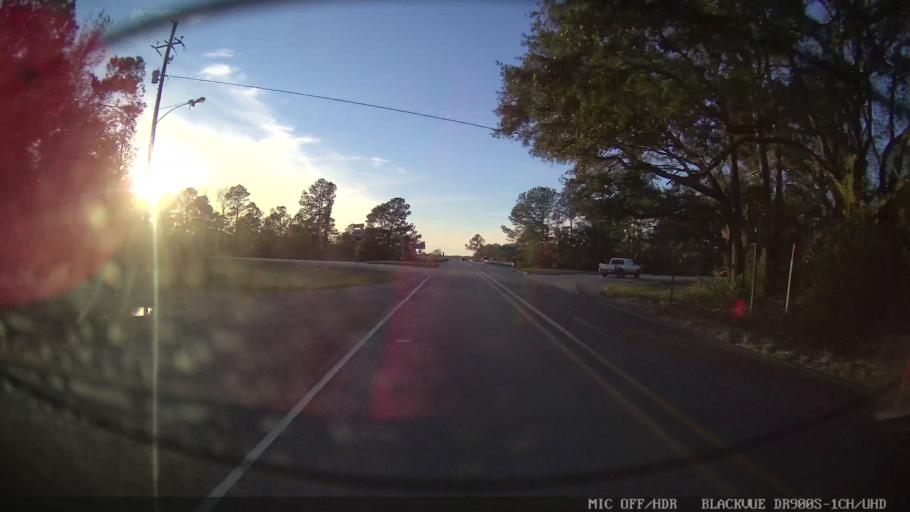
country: US
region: Mississippi
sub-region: Lamar County
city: Lumberton
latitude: 31.0006
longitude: -89.4175
